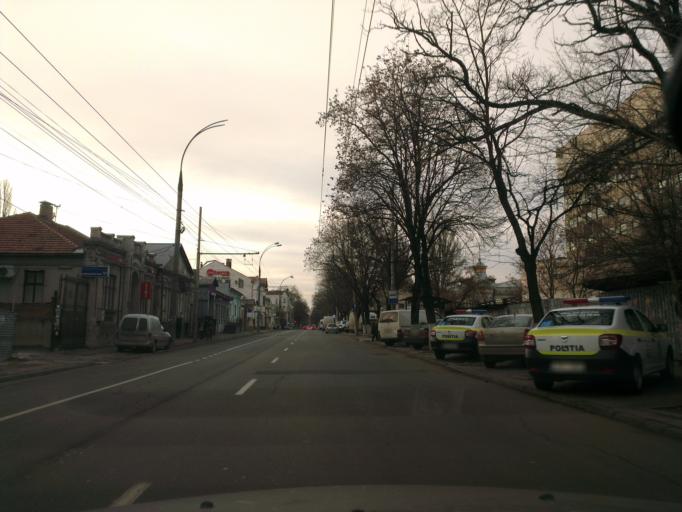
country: MD
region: Chisinau
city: Chisinau
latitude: 47.0211
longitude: 28.8289
